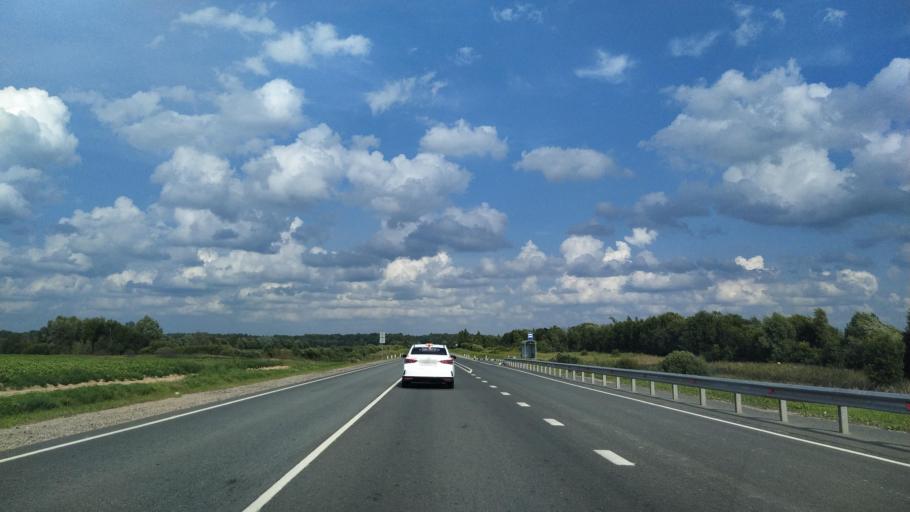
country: RU
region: Novgorod
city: Sol'tsy
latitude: 58.1350
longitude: 30.3887
